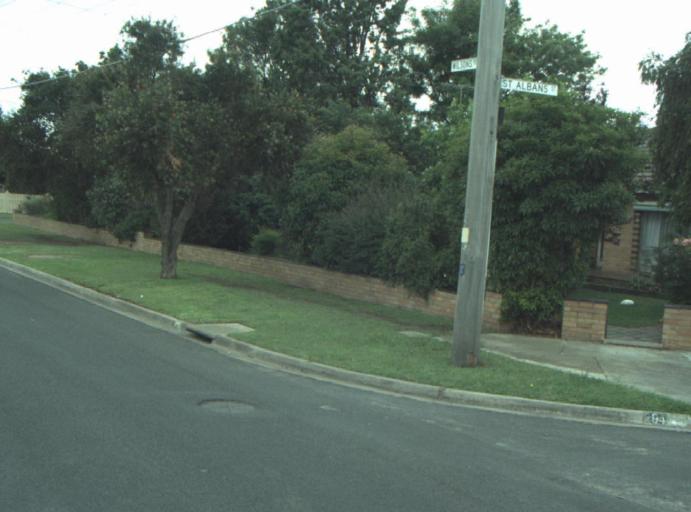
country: AU
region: Victoria
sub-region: Greater Geelong
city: Breakwater
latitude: -38.1857
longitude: 144.3887
